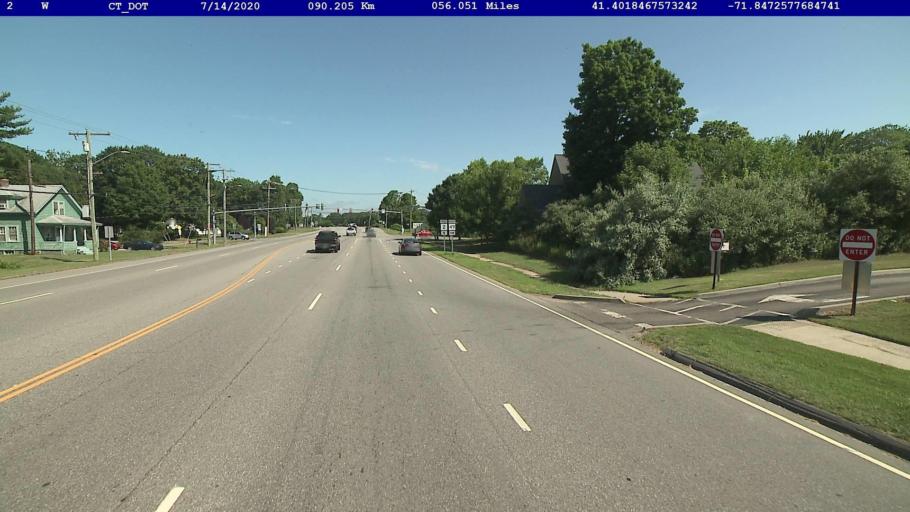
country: US
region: Connecticut
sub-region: New London County
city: Pawcatuck
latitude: 41.4018
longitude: -71.8472
